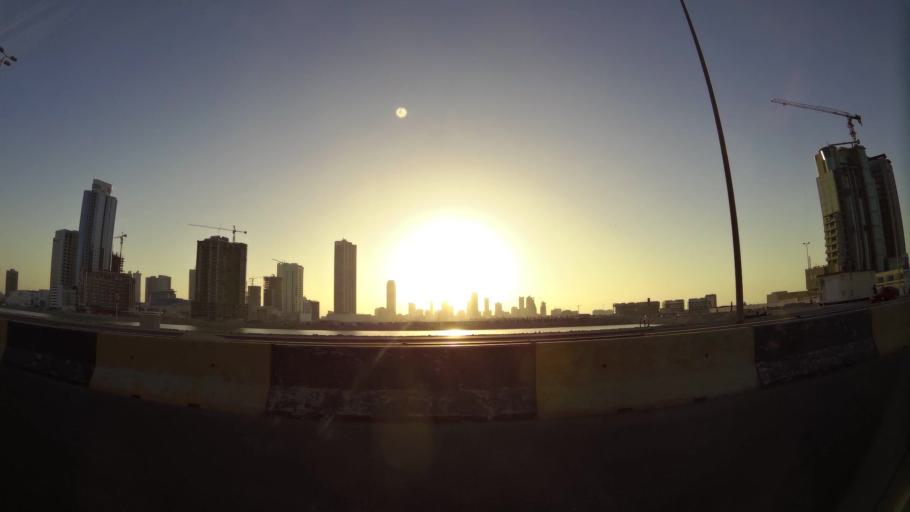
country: BH
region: Manama
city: Jidd Hafs
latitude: 26.2404
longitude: 50.5597
